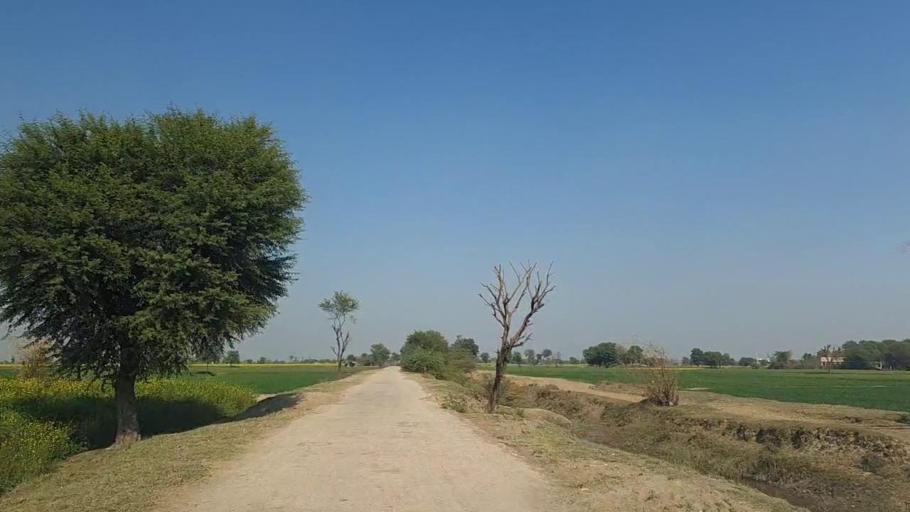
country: PK
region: Sindh
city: Shahpur Chakar
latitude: 26.1882
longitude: 68.6042
